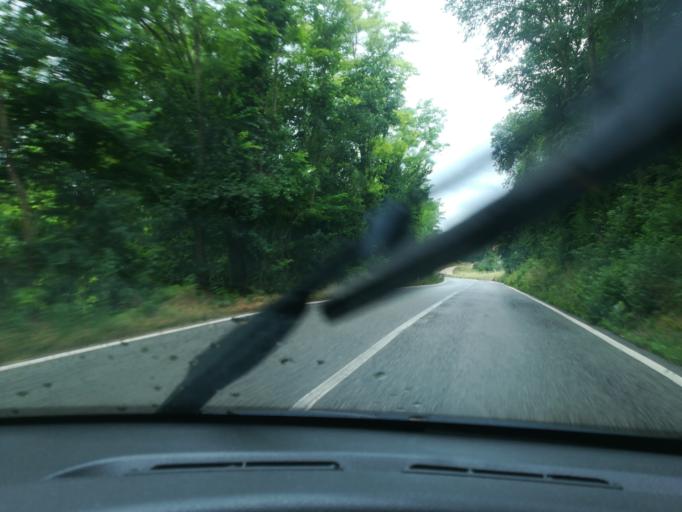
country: IT
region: The Marches
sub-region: Provincia di Macerata
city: San Ginesio
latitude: 43.0954
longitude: 13.3261
